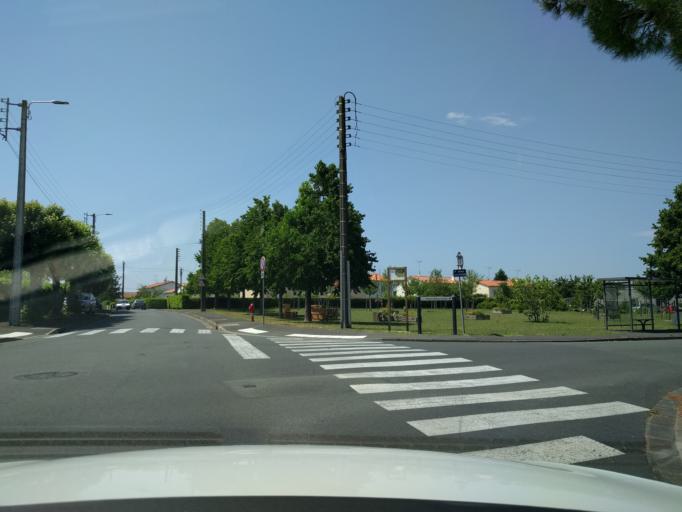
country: FR
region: Poitou-Charentes
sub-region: Departement des Deux-Sevres
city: Niort
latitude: 46.3405
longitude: -0.4808
